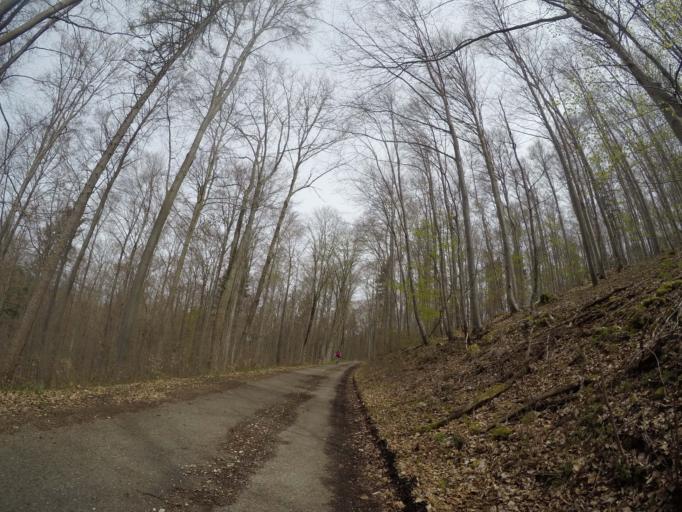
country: DE
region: Baden-Wuerttemberg
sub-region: Regierungsbezirk Stuttgart
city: Neidlingen
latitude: 48.5387
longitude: 9.5616
